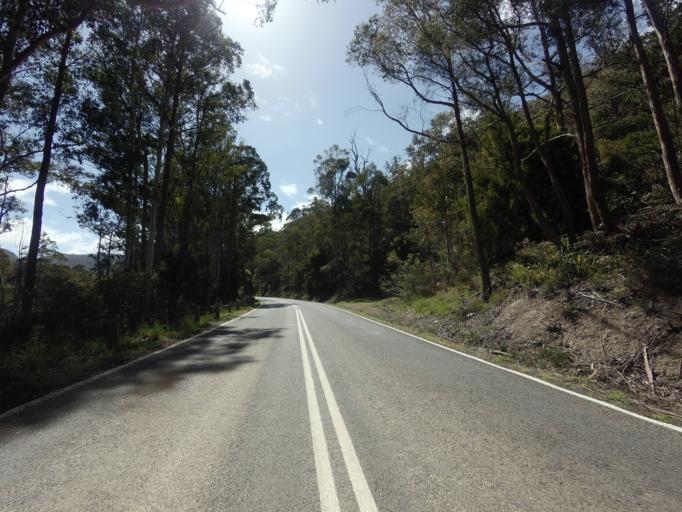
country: AU
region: Tasmania
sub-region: Derwent Valley
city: New Norfolk
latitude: -42.6940
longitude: 146.7141
